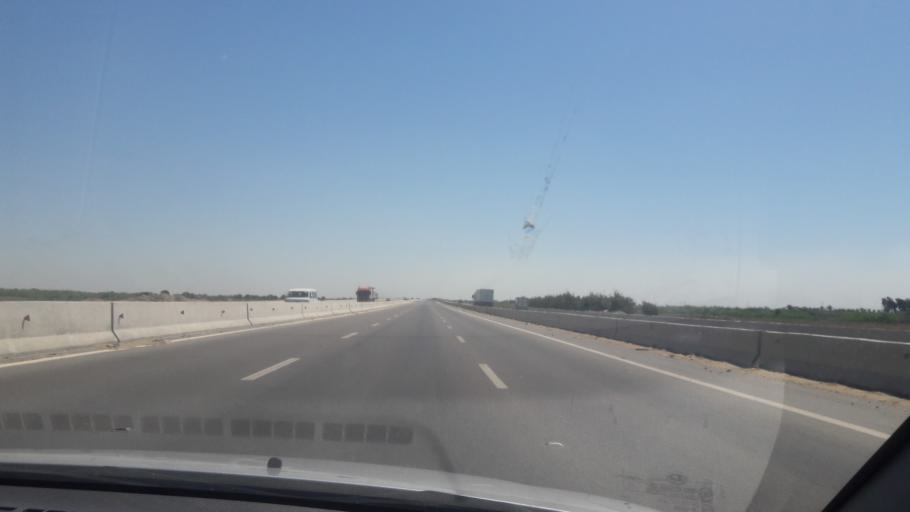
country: EG
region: Muhafazat ad Daqahliyah
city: Al Matariyah
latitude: 30.9099
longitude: 32.1871
